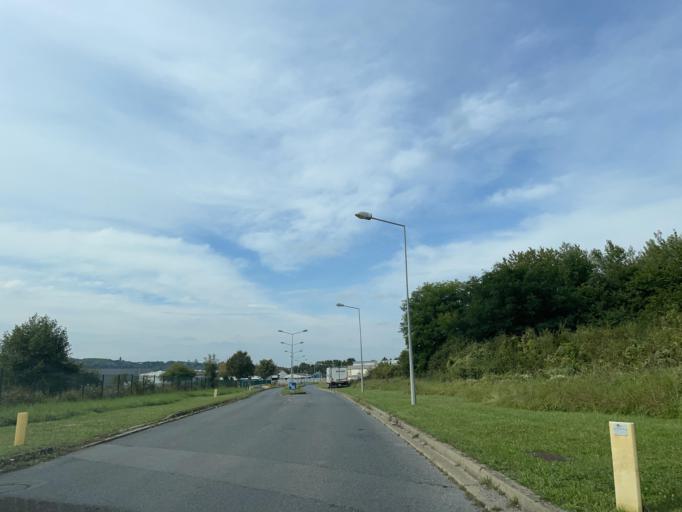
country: FR
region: Ile-de-France
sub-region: Departement de Seine-et-Marne
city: Coulommiers
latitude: 48.8051
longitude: 3.0983
